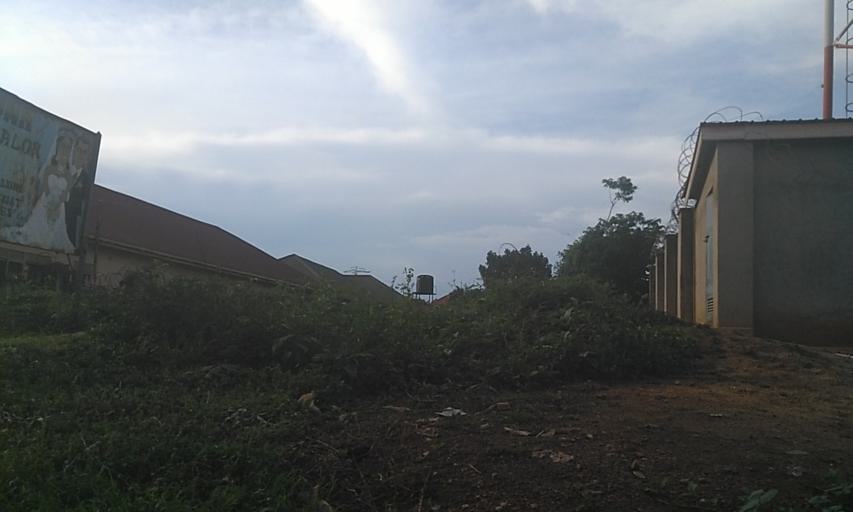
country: UG
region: Central Region
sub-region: Wakiso District
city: Kajansi
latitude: 0.2722
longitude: 32.5221
